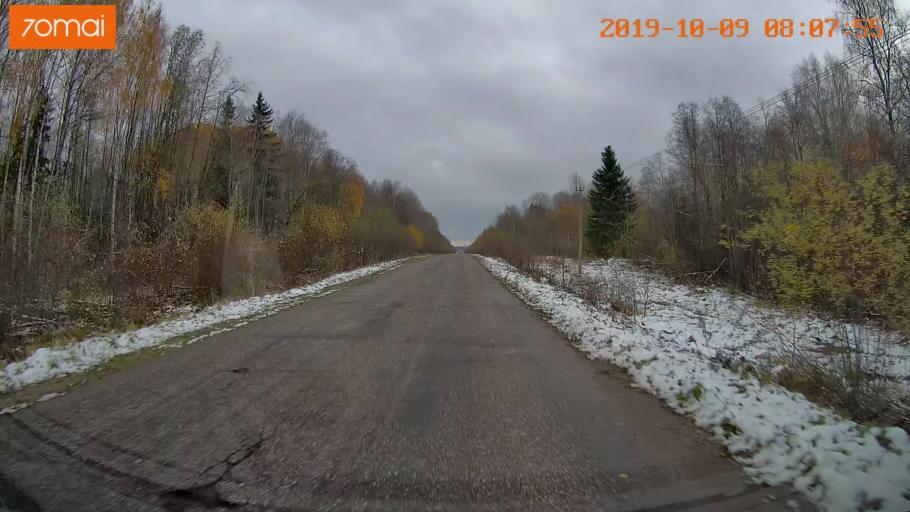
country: RU
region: Jaroslavl
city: Kukoboy
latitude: 58.7008
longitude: 40.0875
